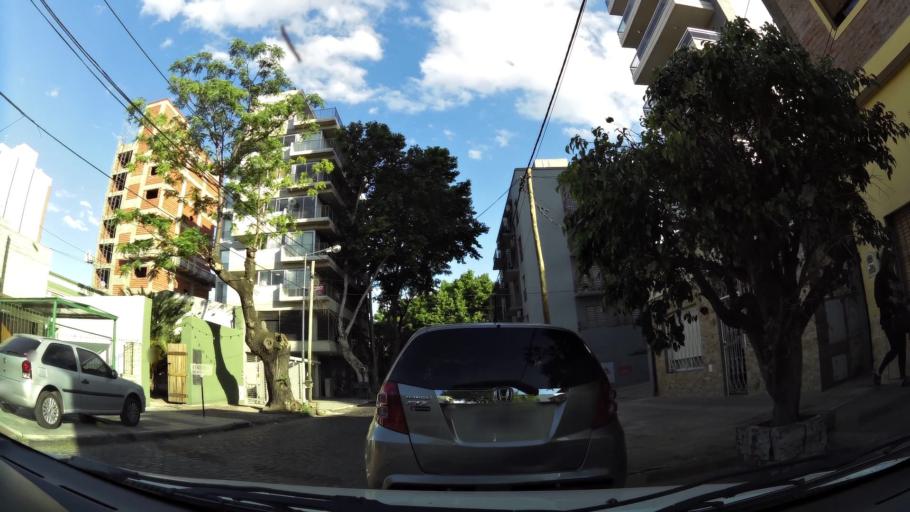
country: AR
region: Buenos Aires
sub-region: Partido de General San Martin
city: General San Martin
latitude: -34.5506
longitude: -58.5511
